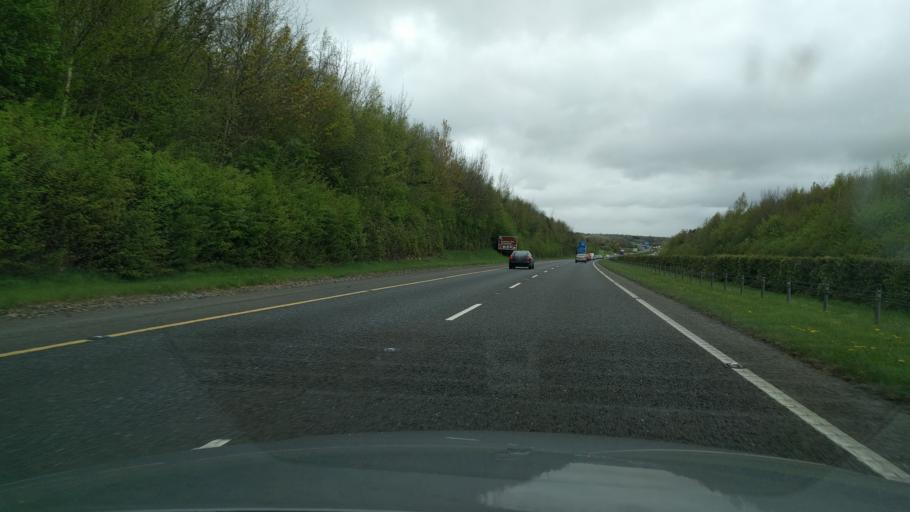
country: IE
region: Leinster
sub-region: An Mhi
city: Stamullin
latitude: 53.6229
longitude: -6.2478
